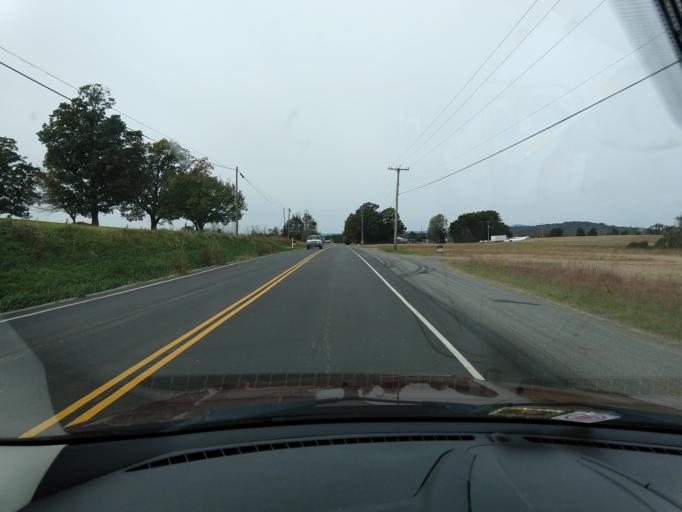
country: US
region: Virginia
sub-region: Franklin County
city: Union Hall
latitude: 36.9864
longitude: -79.7385
